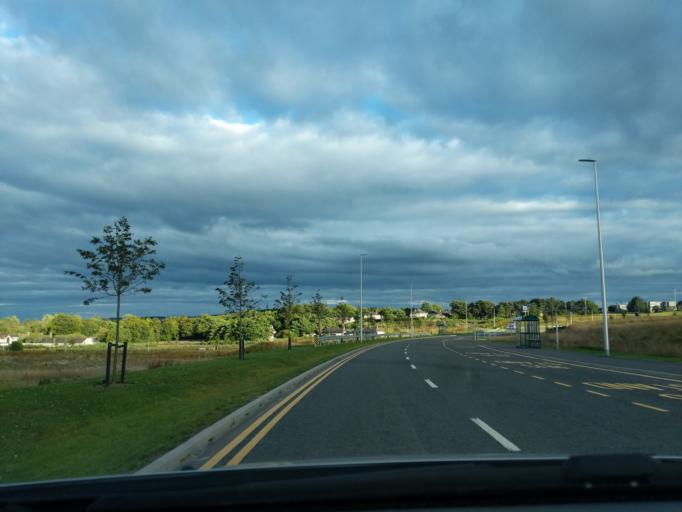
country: GB
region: Scotland
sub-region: Aberdeen City
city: Dyce
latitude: 57.1872
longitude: -2.1881
